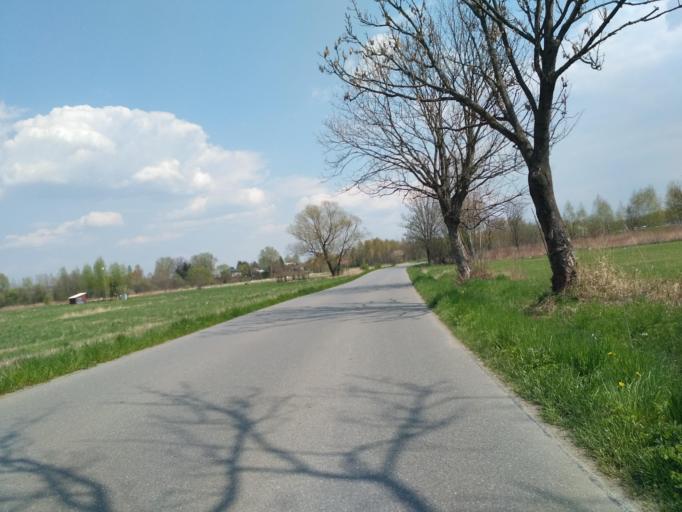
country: PL
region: Subcarpathian Voivodeship
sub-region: Powiat jasielski
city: Tarnowiec
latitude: 49.7375
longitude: 21.5270
